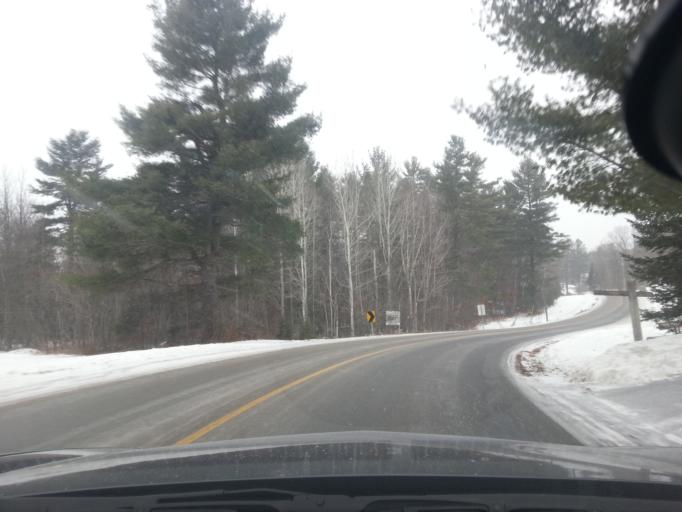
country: CA
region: Ontario
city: Arnprior
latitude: 45.3226
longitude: -76.3256
